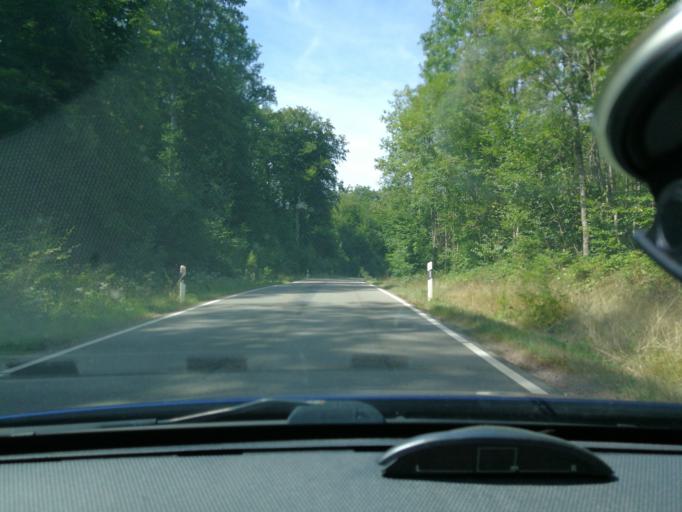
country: DE
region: Rheinland-Pfalz
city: Sehlem
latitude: 49.9057
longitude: 6.8216
